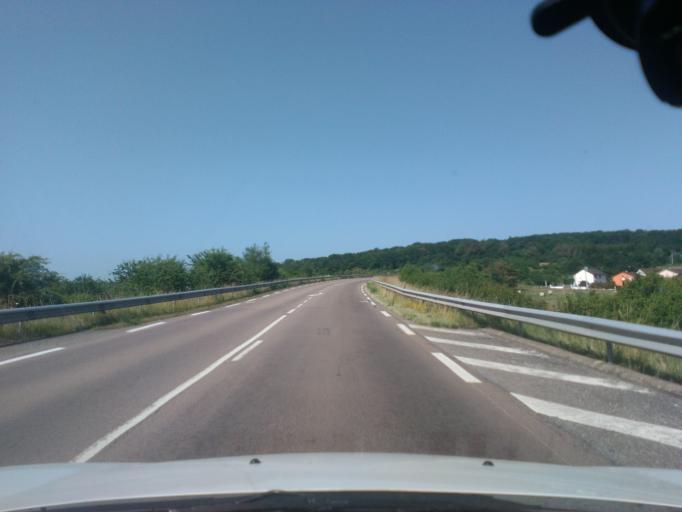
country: FR
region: Lorraine
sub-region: Departement des Vosges
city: Mirecourt
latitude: 48.3069
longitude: 6.0388
